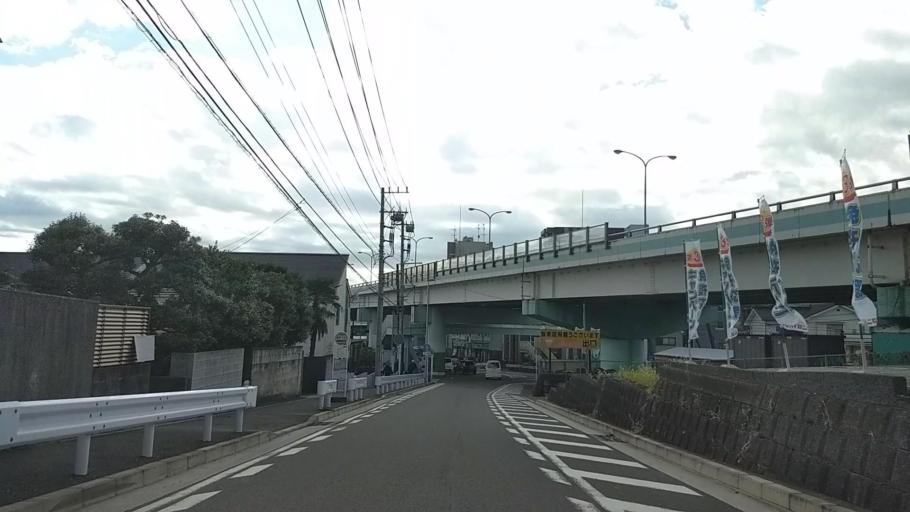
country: JP
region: Kanagawa
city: Yokohama
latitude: 35.4783
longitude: 139.6018
